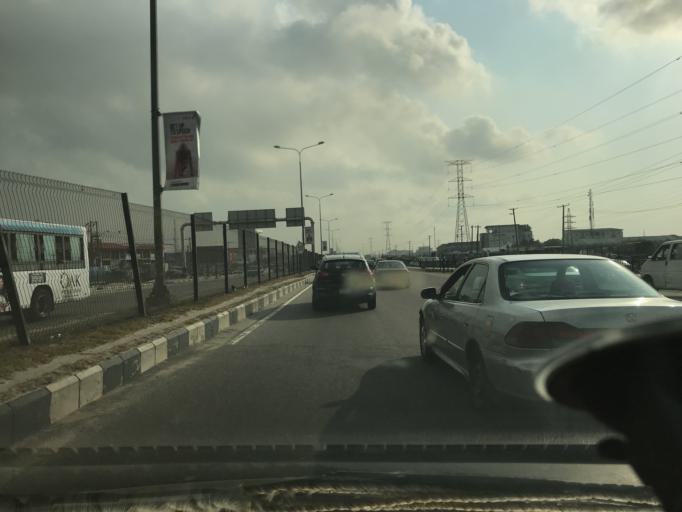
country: NG
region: Lagos
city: Ikoyi
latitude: 6.4369
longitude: 3.5094
